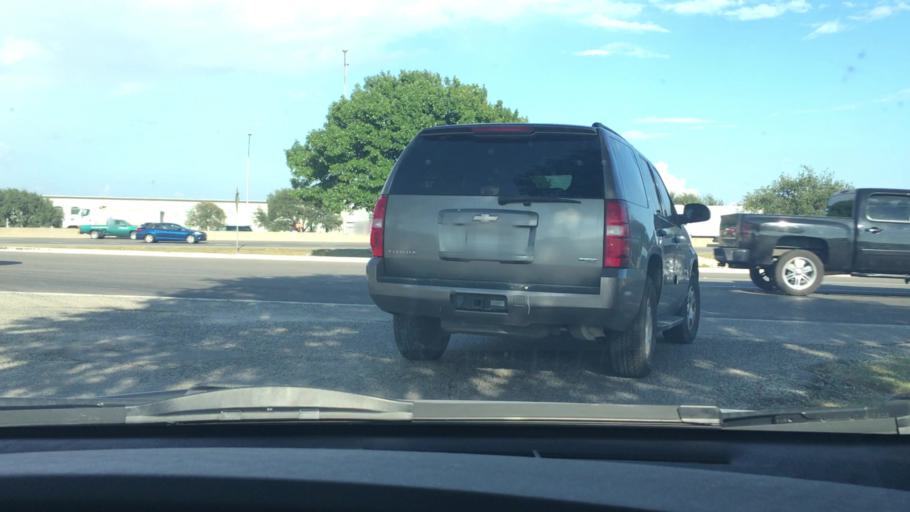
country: US
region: Texas
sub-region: Williamson County
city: Round Rock
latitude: 30.5188
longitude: -97.6892
